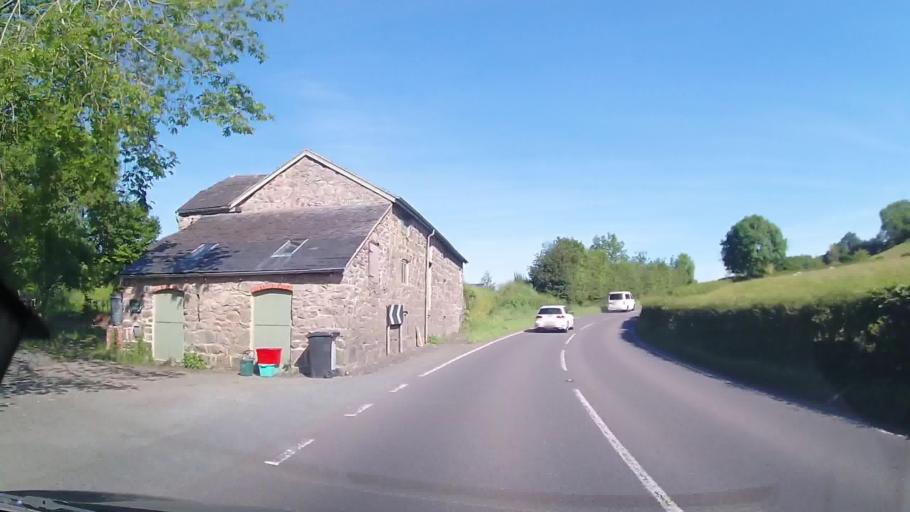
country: GB
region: Wales
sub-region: Sir Powys
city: Welshpool
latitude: 52.6547
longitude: -3.2578
